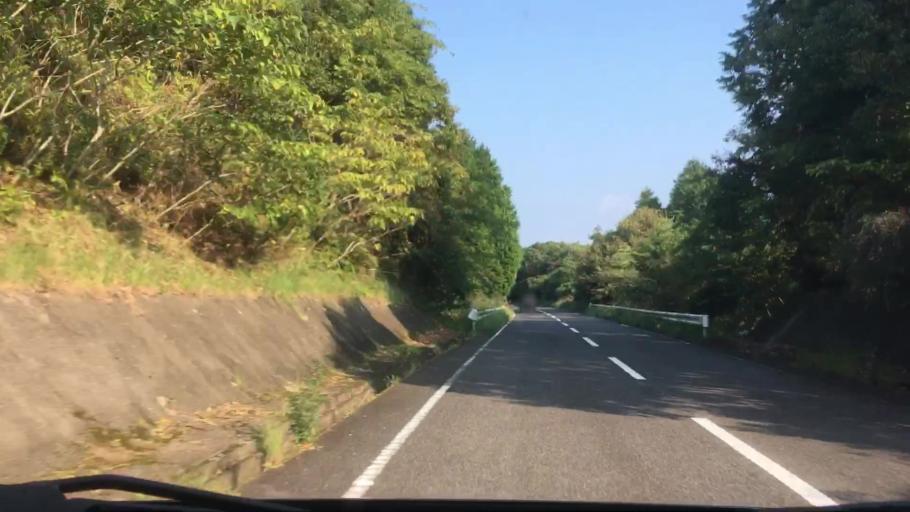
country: JP
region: Nagasaki
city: Sasebo
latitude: 33.0295
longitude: 129.6900
